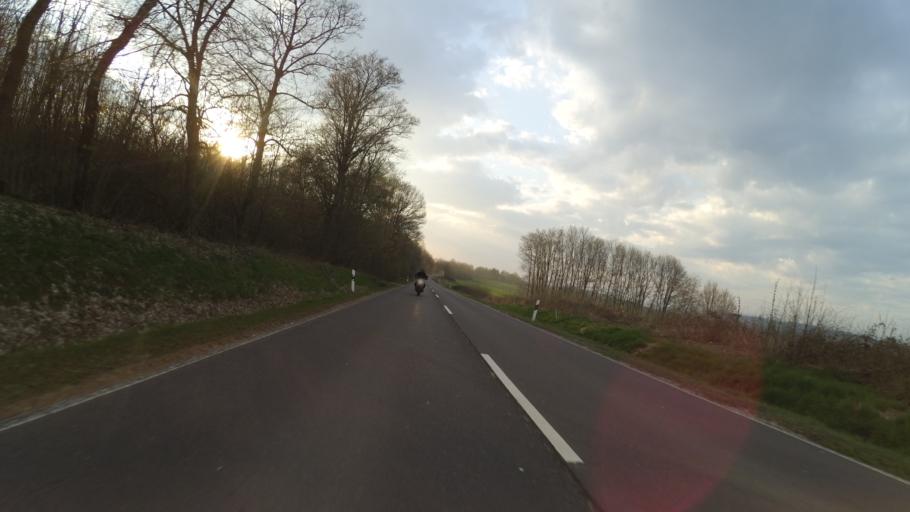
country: DE
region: Rheinland-Pfalz
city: Longkamp
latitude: 49.8758
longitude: 7.1106
